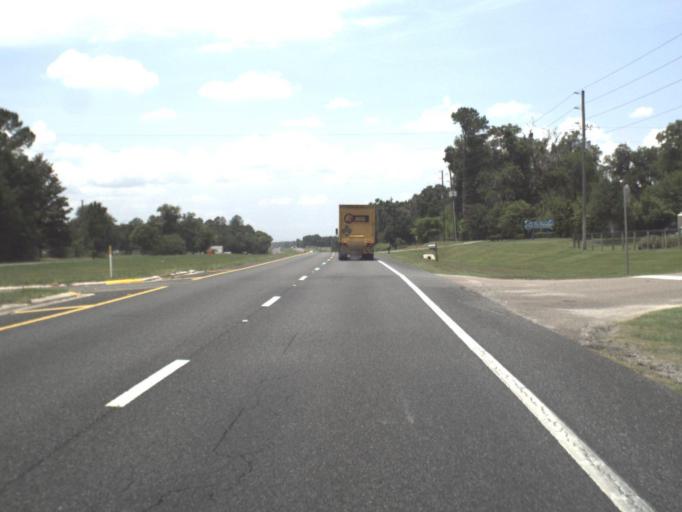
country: US
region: Florida
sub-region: Alachua County
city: Newberry
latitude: 29.6546
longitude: -82.5488
